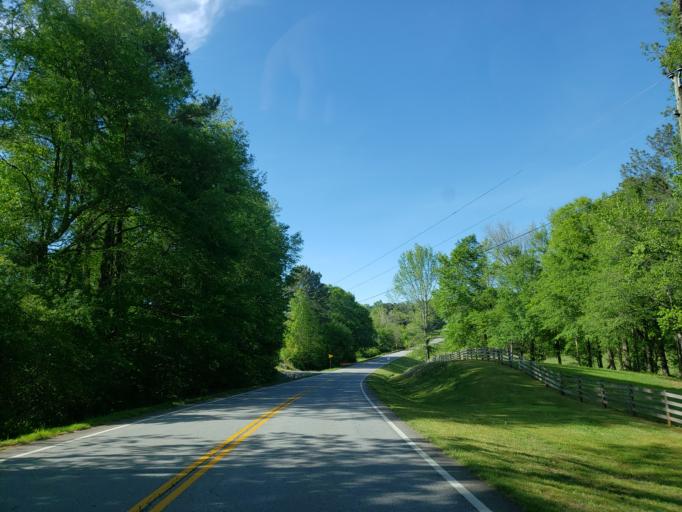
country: US
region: Georgia
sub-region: Haralson County
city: Tallapoosa
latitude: 33.7043
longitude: -85.2713
